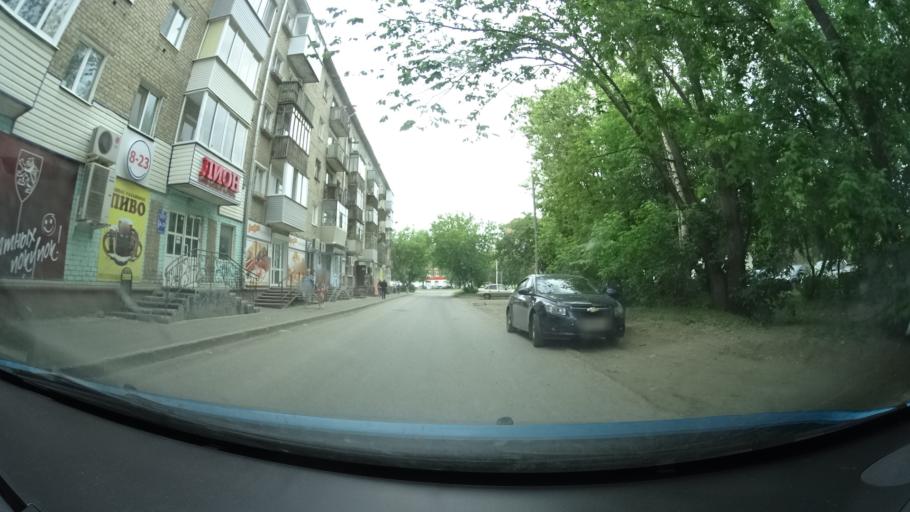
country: RU
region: Perm
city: Perm
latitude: 58.0203
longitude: 56.2755
